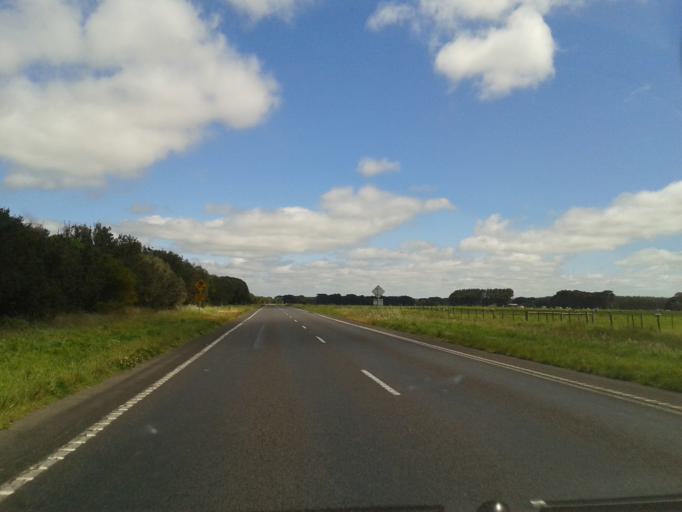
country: AU
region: Victoria
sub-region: Glenelg
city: Portland
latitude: -38.2473
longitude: 141.8862
